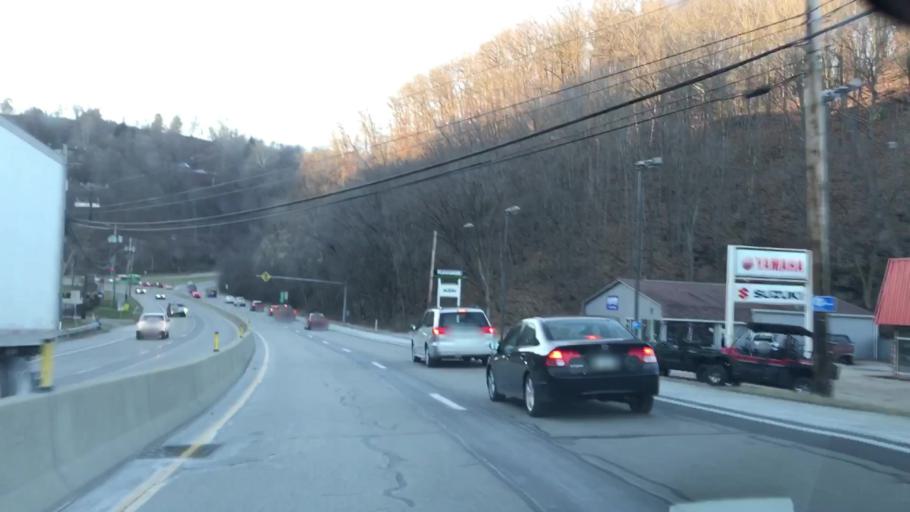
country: US
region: Pennsylvania
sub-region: Allegheny County
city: Sewickley
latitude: 40.5369
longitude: -80.1969
